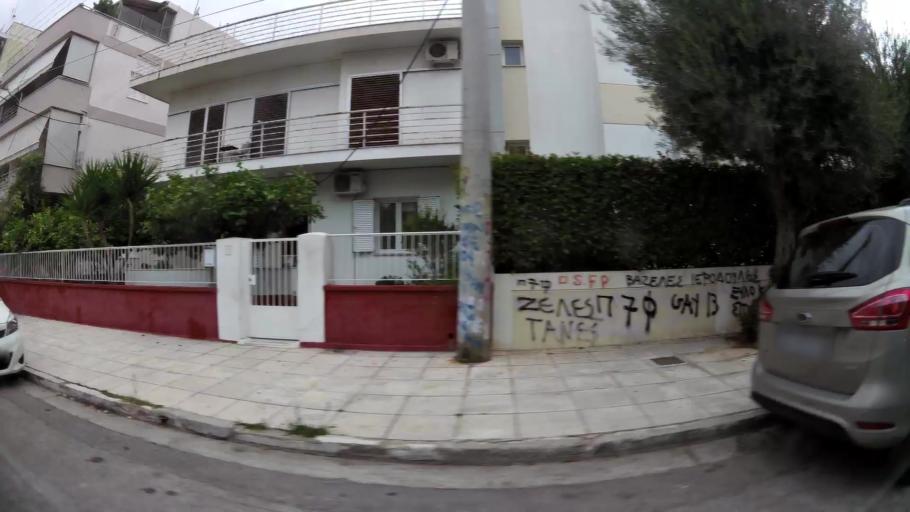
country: GR
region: Attica
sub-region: Nomarchia Athinas
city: Alimos
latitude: 37.9239
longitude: 23.7175
